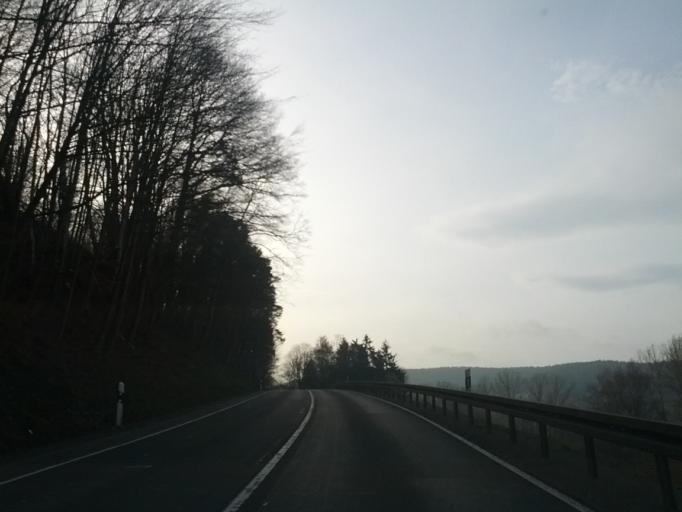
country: DE
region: Thuringia
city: Schwallungen
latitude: 50.6794
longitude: 10.3536
